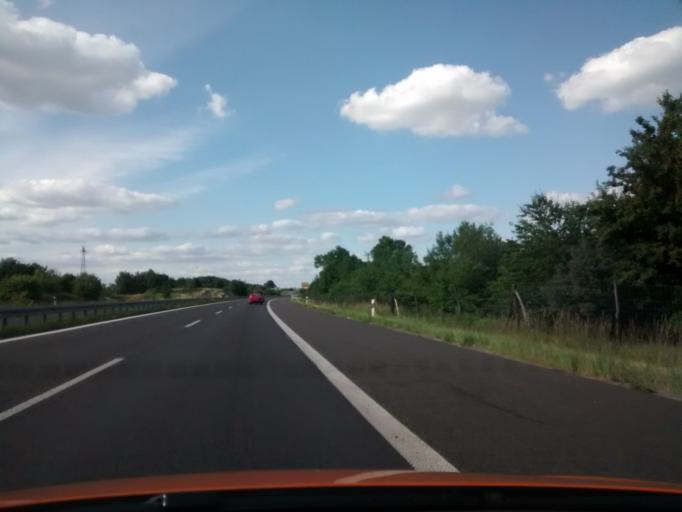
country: DE
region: Brandenburg
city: Grossbeeren
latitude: 52.3414
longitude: 13.2829
